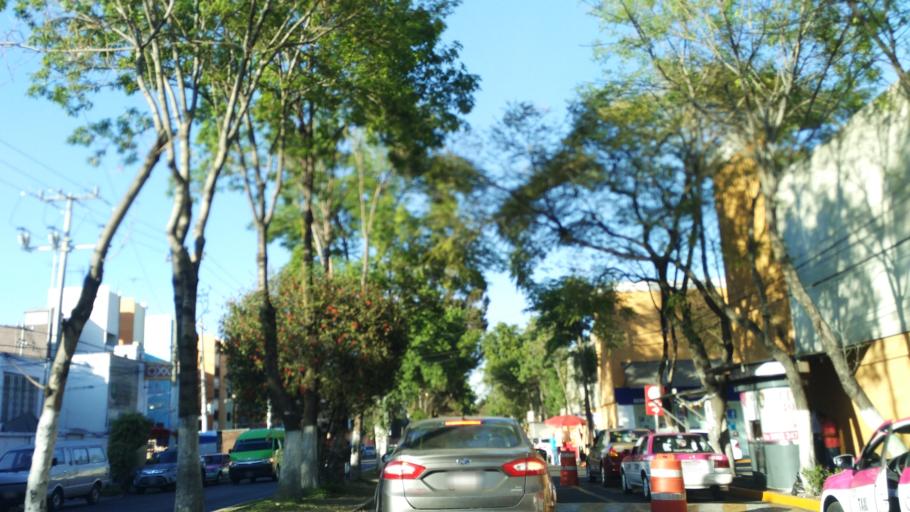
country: MX
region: Mexico City
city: Xochimilco
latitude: 19.2953
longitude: -99.1102
